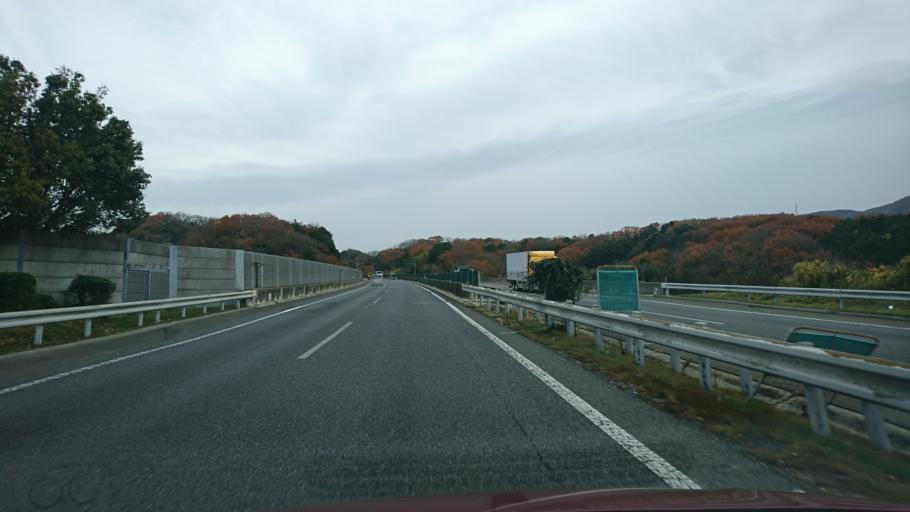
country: JP
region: Hyogo
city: Sandacho
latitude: 34.8207
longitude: 135.1132
